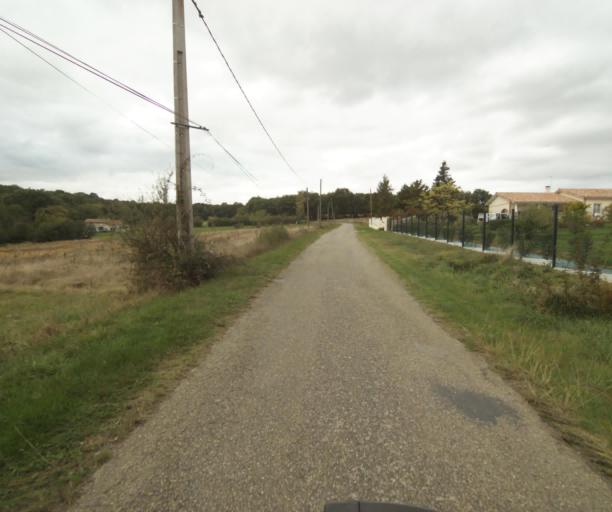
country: FR
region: Midi-Pyrenees
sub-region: Departement du Tarn-et-Garonne
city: Beaumont-de-Lomagne
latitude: 43.8421
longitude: 1.1035
